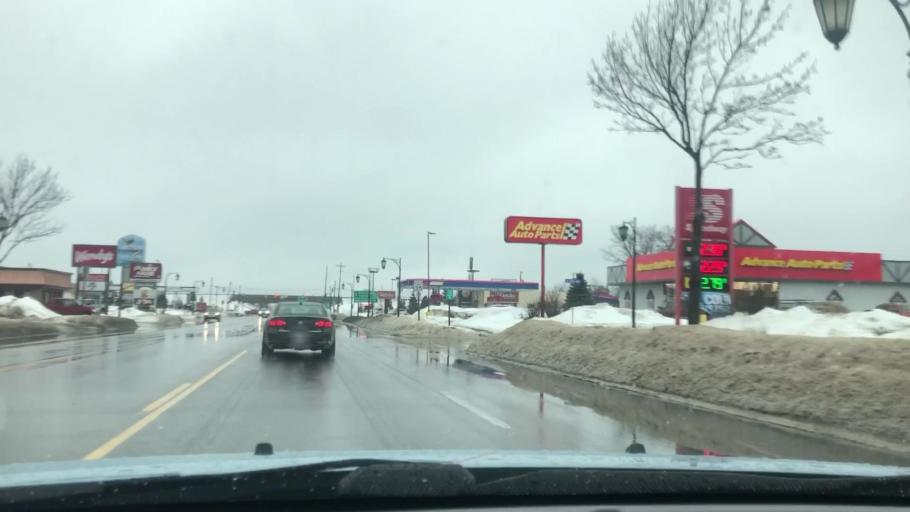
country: US
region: Michigan
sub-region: Otsego County
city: Gaylord
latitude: 45.0274
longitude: -84.6835
